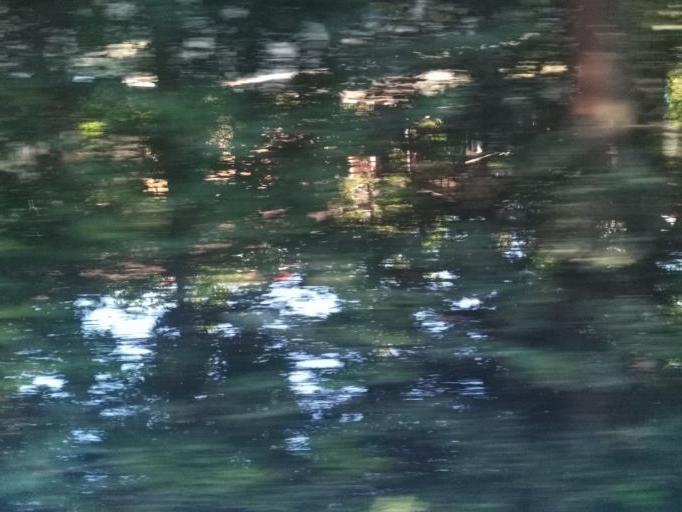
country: TZ
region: Dar es Salaam
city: Magomeni
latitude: -6.7661
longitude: 39.2541
